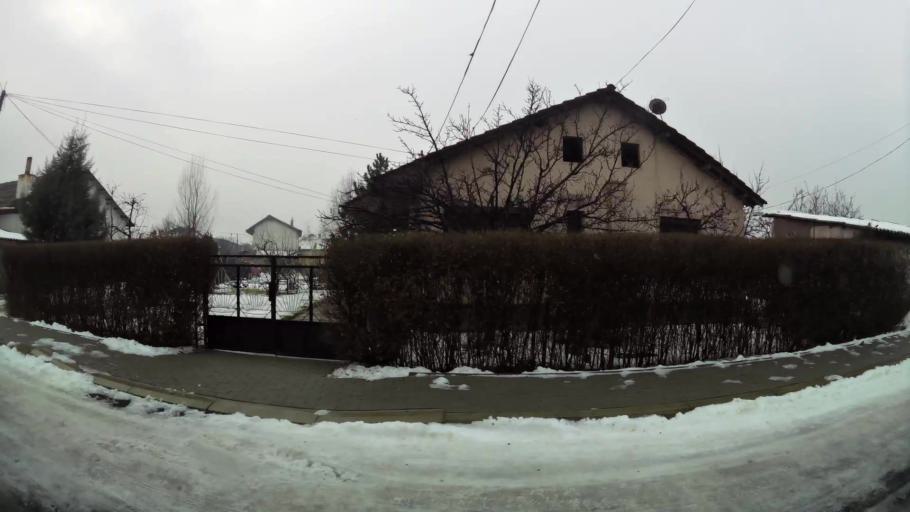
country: MK
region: Petrovec
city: Petrovec
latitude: 41.9420
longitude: 21.6118
